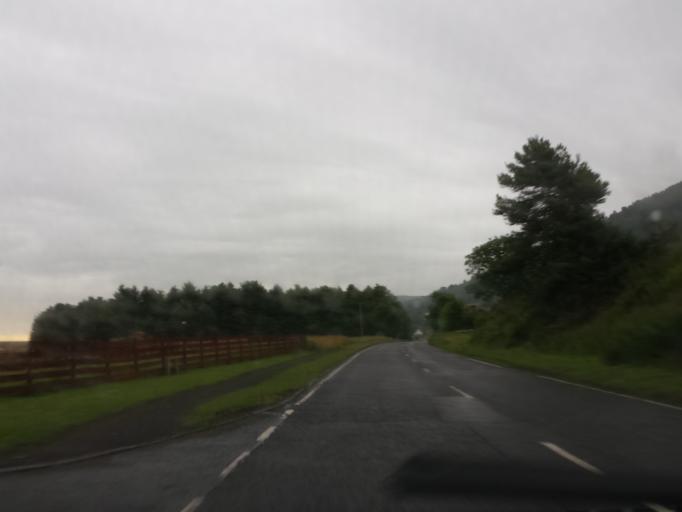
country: GB
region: Scotland
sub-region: Perth and Kinross
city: Abernethy
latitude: 56.3280
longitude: -3.3444
